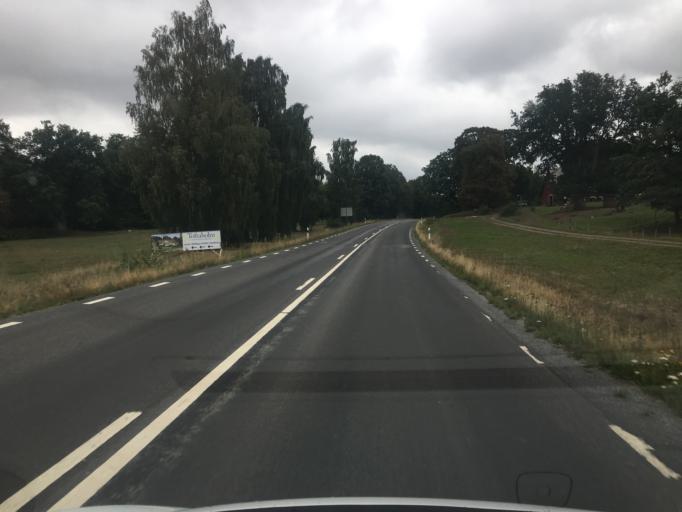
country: SE
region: Kronoberg
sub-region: Ljungby Kommun
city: Lagan
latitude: 57.0258
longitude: 14.0156
